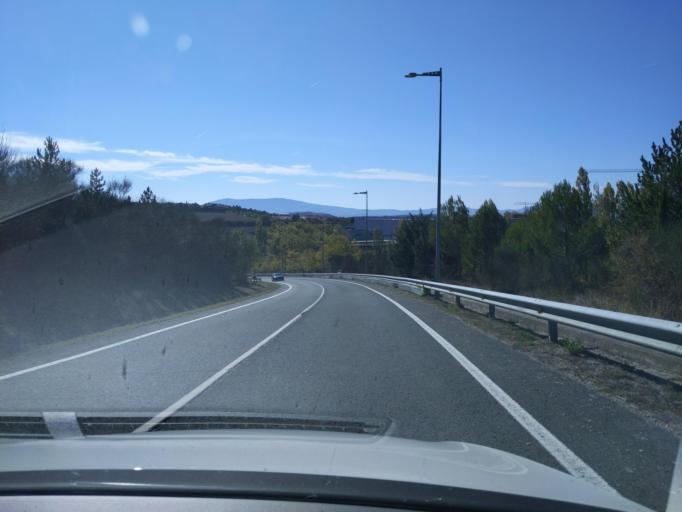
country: ES
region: Navarre
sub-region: Provincia de Navarra
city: Egues-Uharte
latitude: 42.8327
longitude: -1.5708
